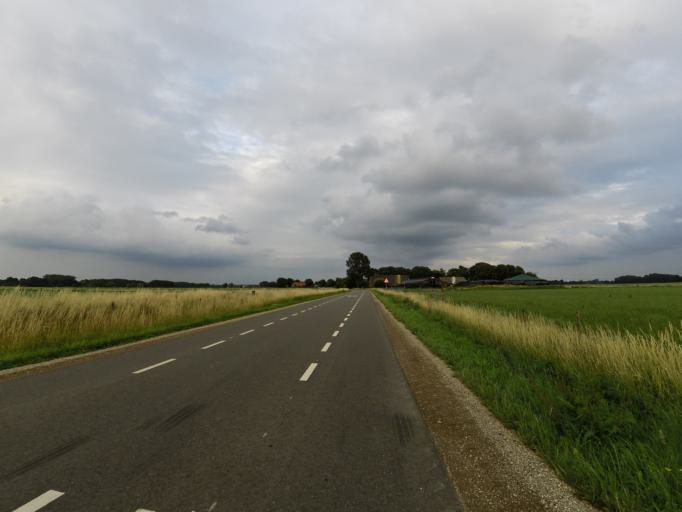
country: NL
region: Gelderland
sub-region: Gemeente Doesburg
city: Doesburg
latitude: 51.9886
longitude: 6.1722
